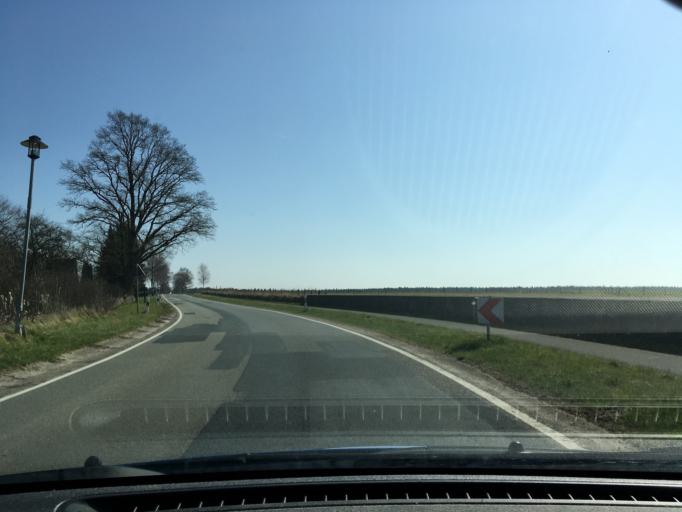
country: DE
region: Lower Saxony
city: Rehlingen
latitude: 53.0991
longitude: 10.2595
